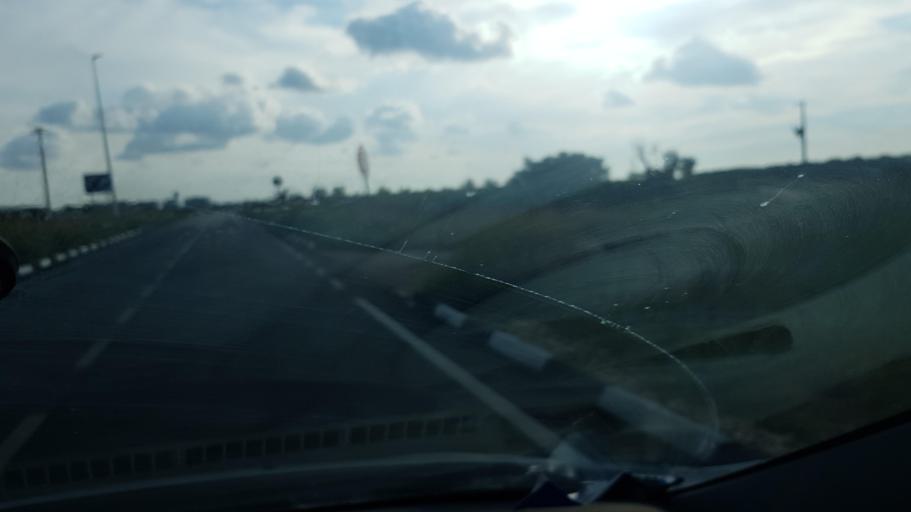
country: IT
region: Apulia
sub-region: Provincia di Brindisi
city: San Donaci
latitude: 40.4385
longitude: 17.9545
